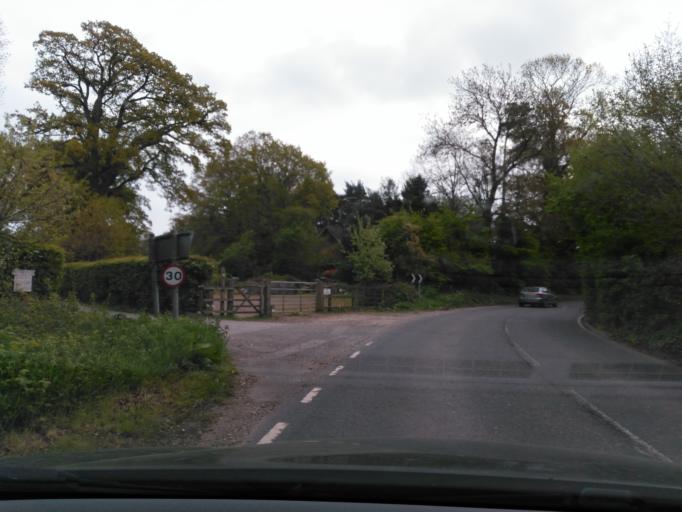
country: GB
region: England
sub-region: Hampshire
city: Tadley
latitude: 51.3272
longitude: -1.0801
